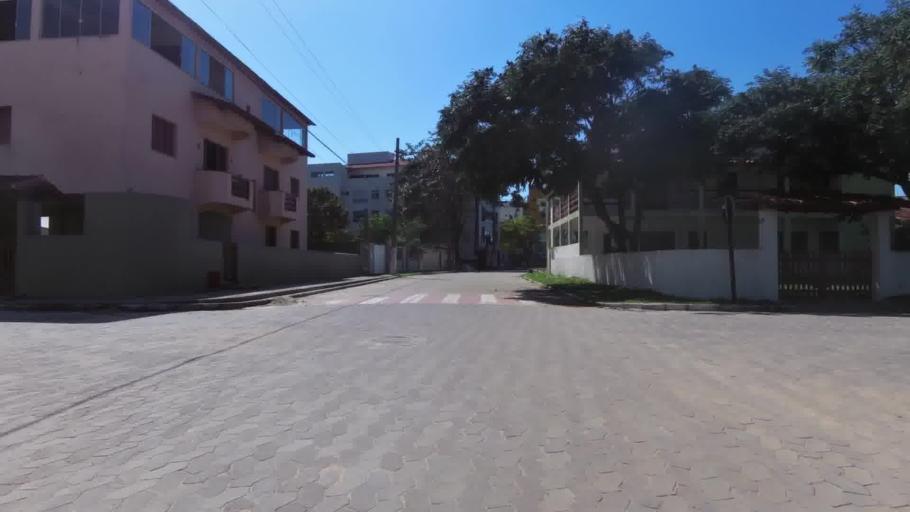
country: BR
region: Espirito Santo
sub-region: Piuma
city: Piuma
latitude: -20.8339
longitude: -40.6264
